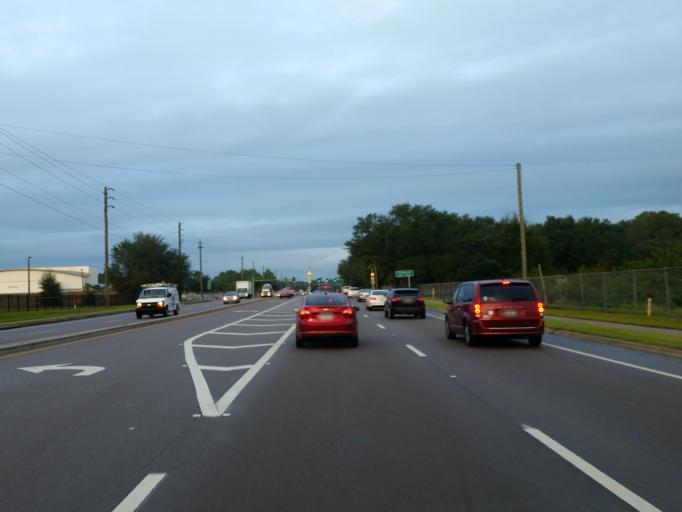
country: US
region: Florida
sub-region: Hillsborough County
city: Riverview
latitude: 27.8537
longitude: -82.3092
